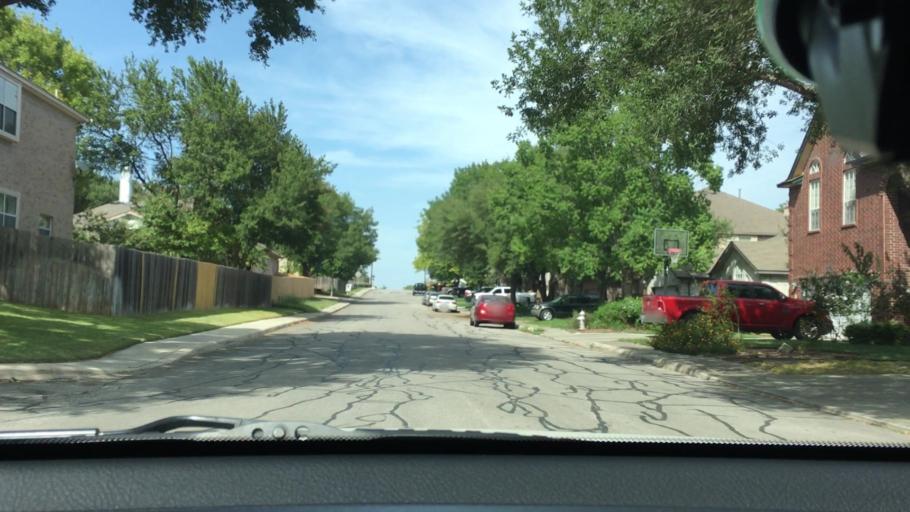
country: US
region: Texas
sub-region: Bexar County
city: Live Oak
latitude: 29.5833
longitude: -98.3802
